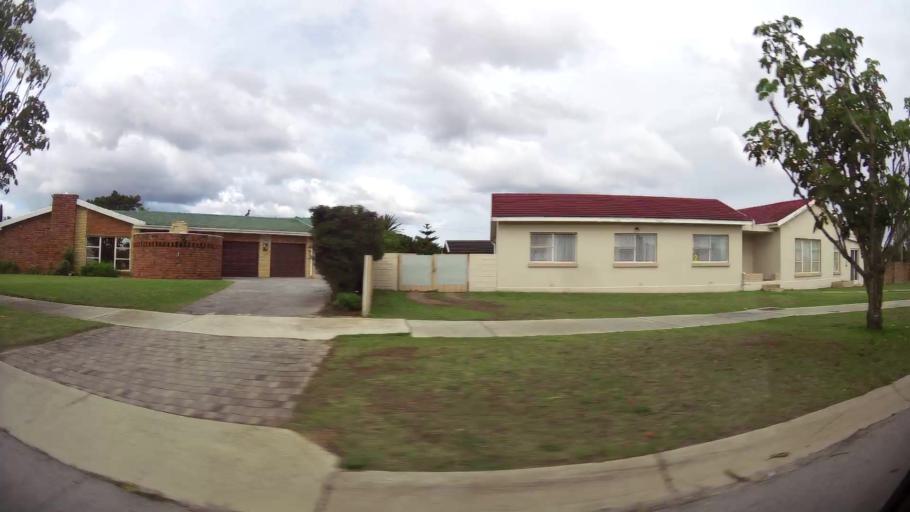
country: ZA
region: Eastern Cape
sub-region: Nelson Mandela Bay Metropolitan Municipality
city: Port Elizabeth
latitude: -33.9380
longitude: 25.5209
